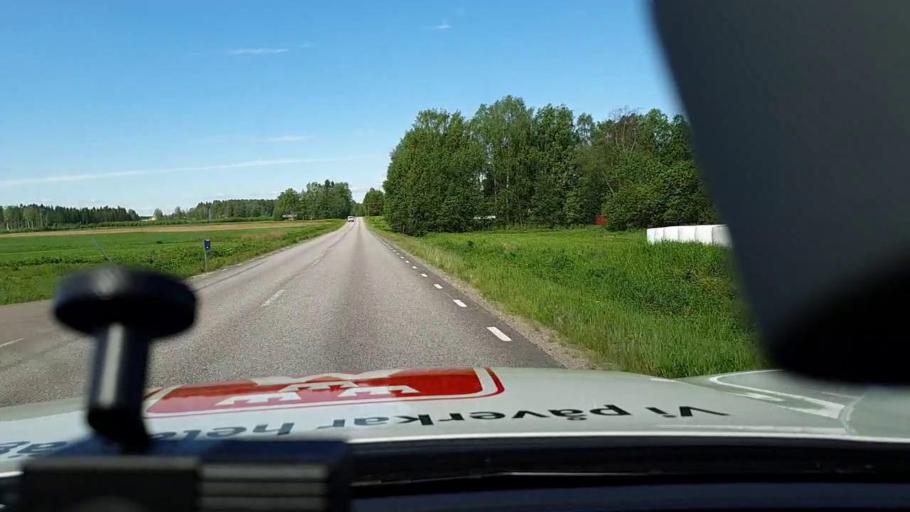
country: SE
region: Norrbotten
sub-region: Lulea Kommun
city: Sodra Sunderbyn
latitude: 65.6528
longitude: 21.8610
